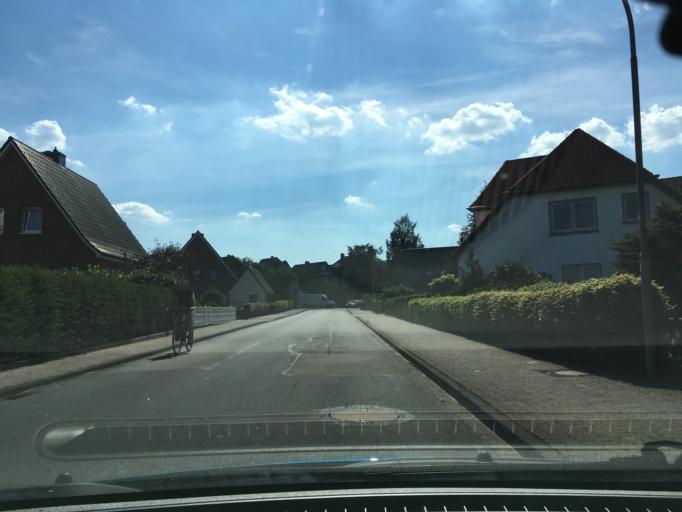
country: DE
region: Lower Saxony
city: Seevetal
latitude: 53.3875
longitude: 9.9900
